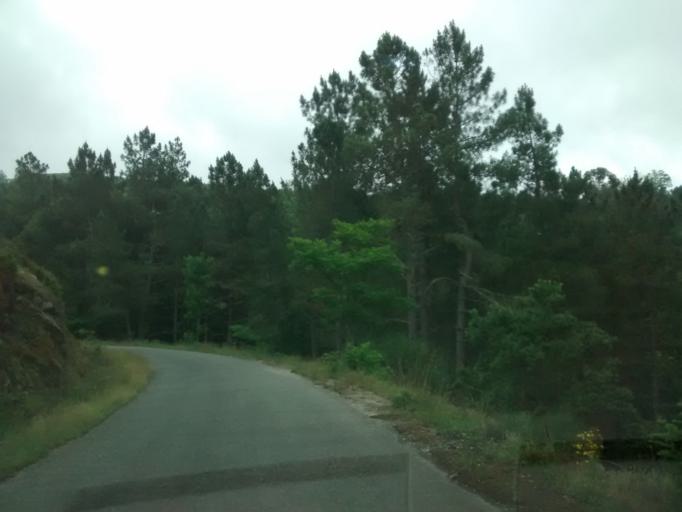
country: ES
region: Galicia
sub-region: Provincia de Ourense
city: Castro Caldelas
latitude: 42.4083
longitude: -7.3937
